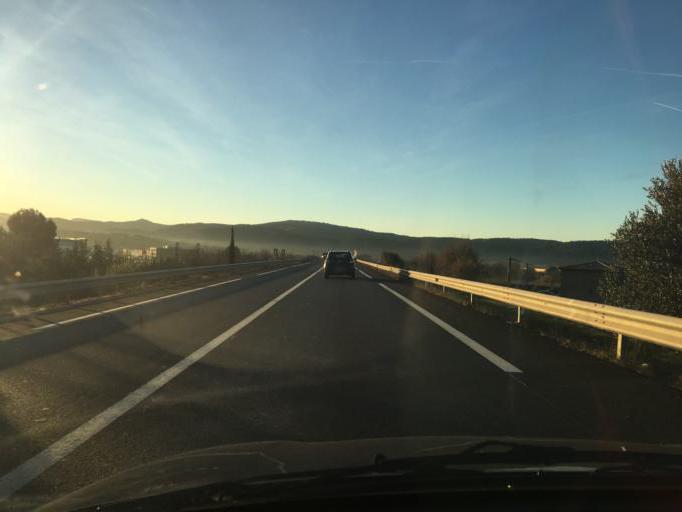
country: FR
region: Provence-Alpes-Cote d'Azur
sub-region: Departement du Var
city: Les Arcs
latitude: 43.4586
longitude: 6.4882
